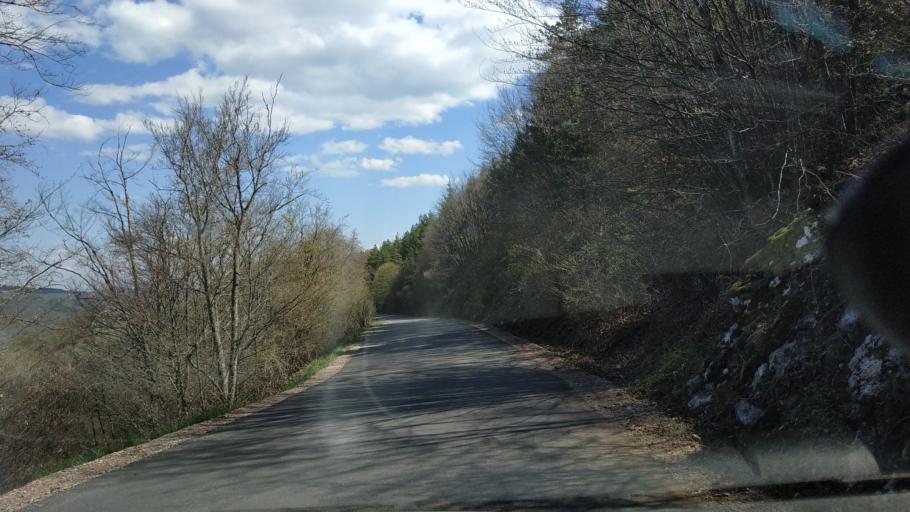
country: RS
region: Central Serbia
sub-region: Zajecarski Okrug
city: Soko Banja
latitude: 43.5869
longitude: 21.8874
